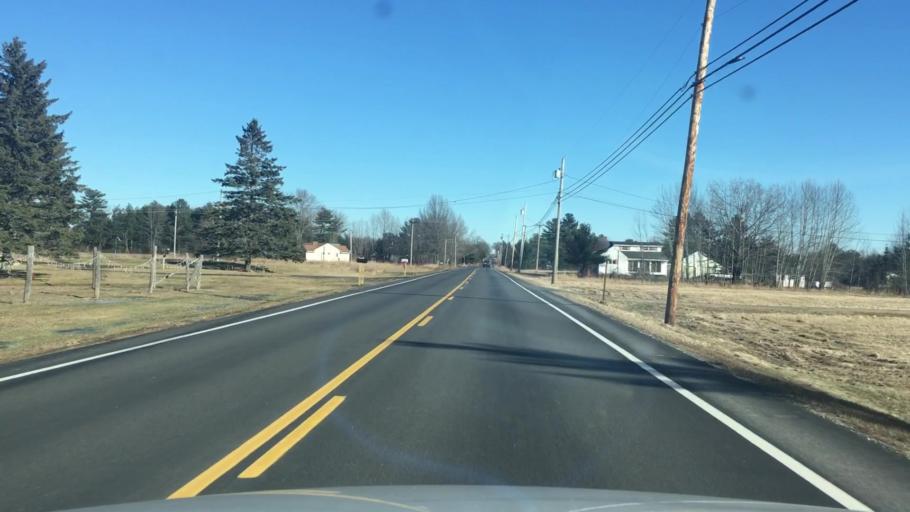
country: US
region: Maine
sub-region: Kennebec County
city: Benton
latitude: 44.6049
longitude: -69.5348
